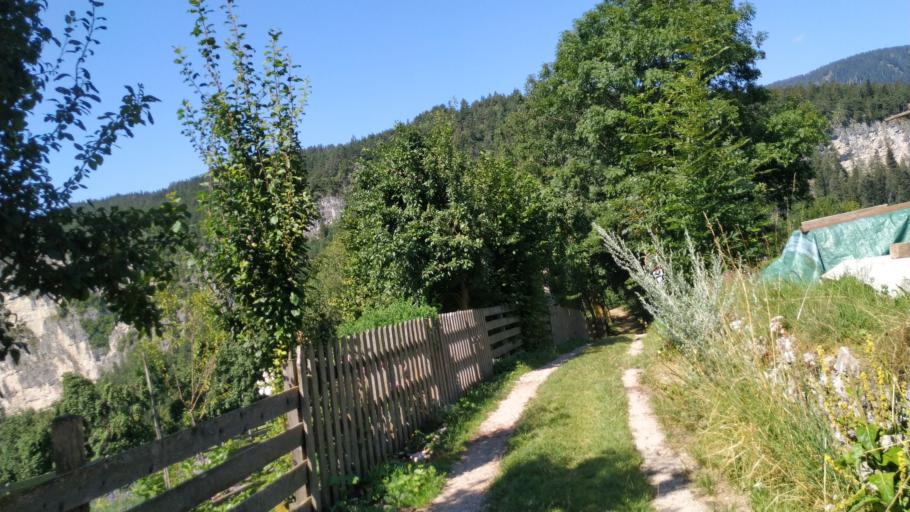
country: IT
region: Trentino-Alto Adige
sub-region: Bolzano
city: San Felice
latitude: 46.4785
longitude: 11.1349
